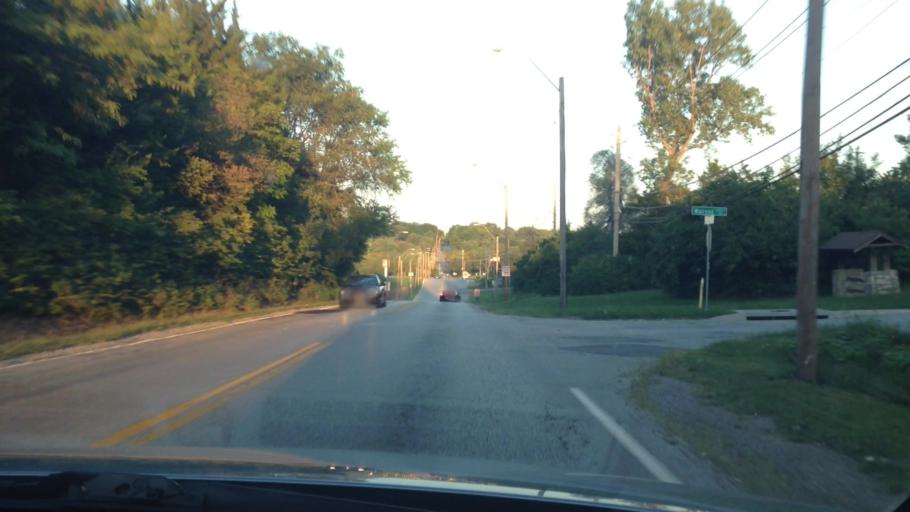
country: US
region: Missouri
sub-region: Jackson County
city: Grandview
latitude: 38.9247
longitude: -94.5540
